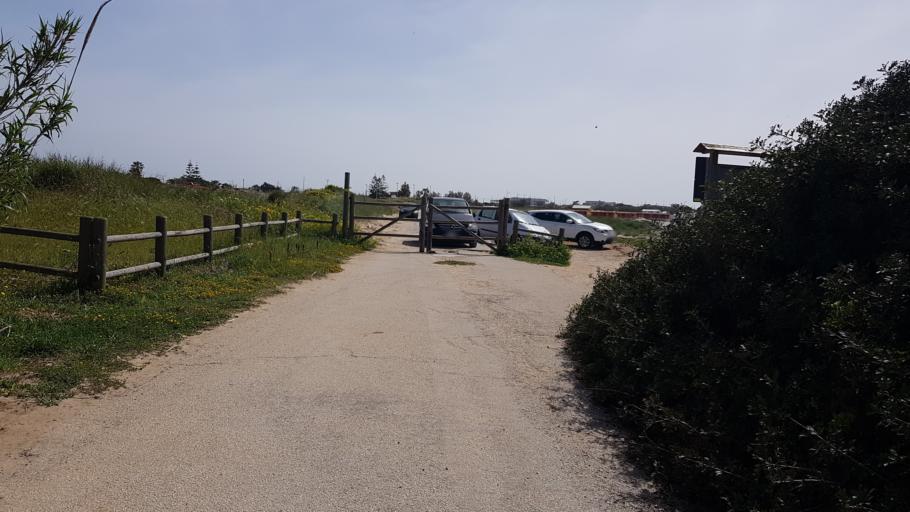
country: IT
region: Apulia
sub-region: Provincia di Brindisi
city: Materdomini
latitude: 40.6830
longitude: 17.9357
